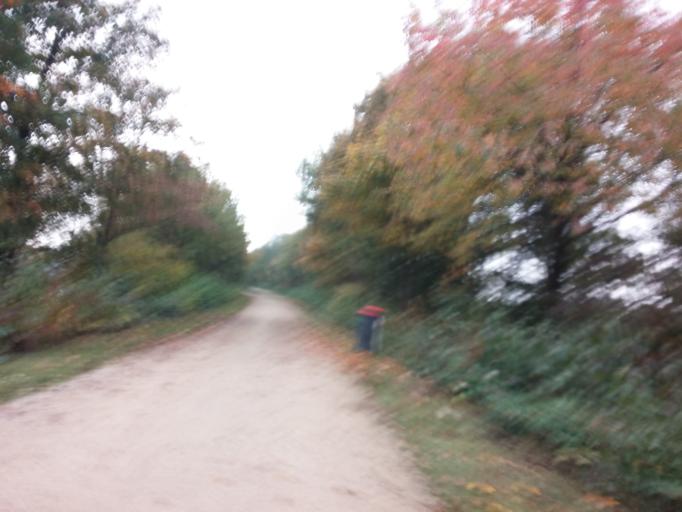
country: DE
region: North Rhine-Westphalia
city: Dorsten
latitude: 51.6657
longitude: 6.9514
